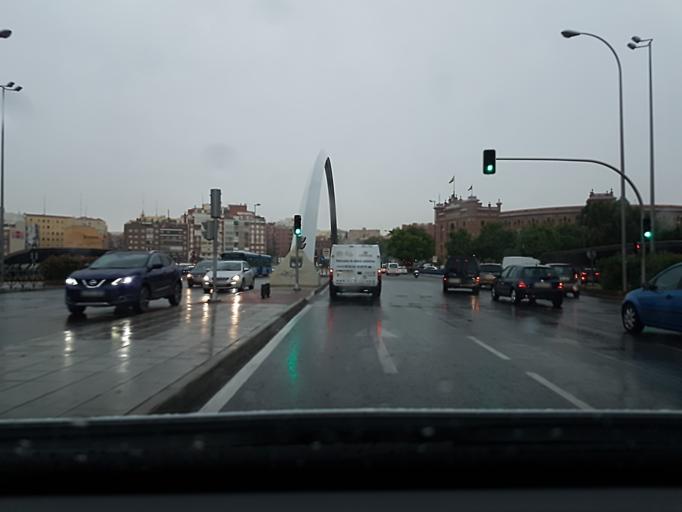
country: ES
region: Madrid
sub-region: Provincia de Madrid
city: Moratalaz
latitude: 40.4316
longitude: -3.6598
